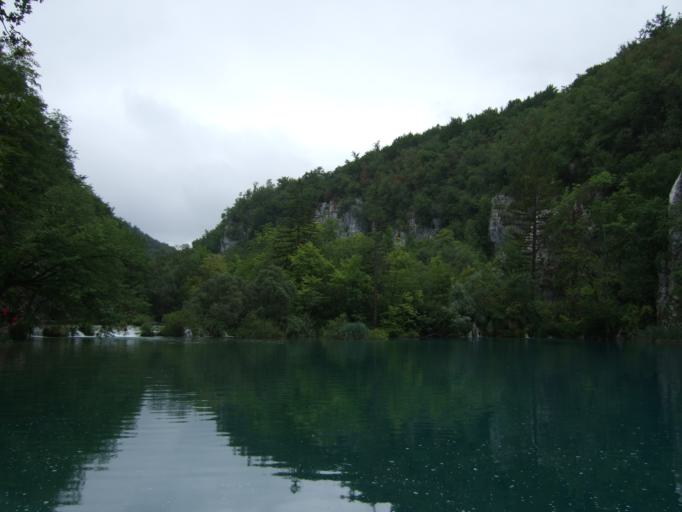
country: HR
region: Licko-Senjska
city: Jezerce
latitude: 44.8988
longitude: 15.6113
